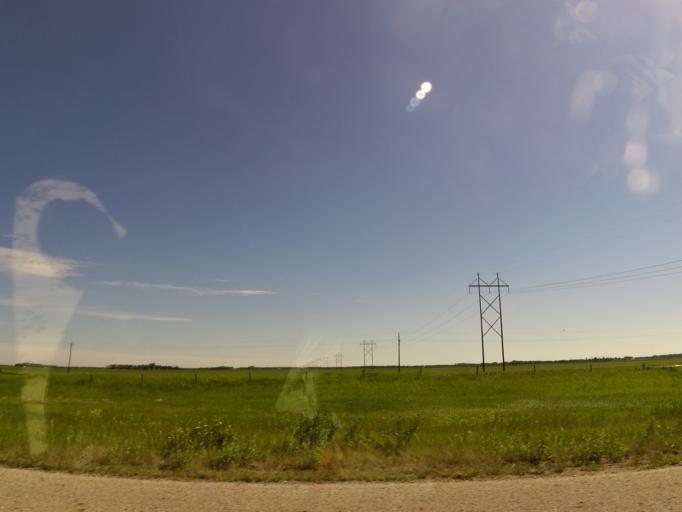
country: US
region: North Dakota
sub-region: Cass County
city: West Fargo
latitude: 46.9659
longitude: -96.8714
